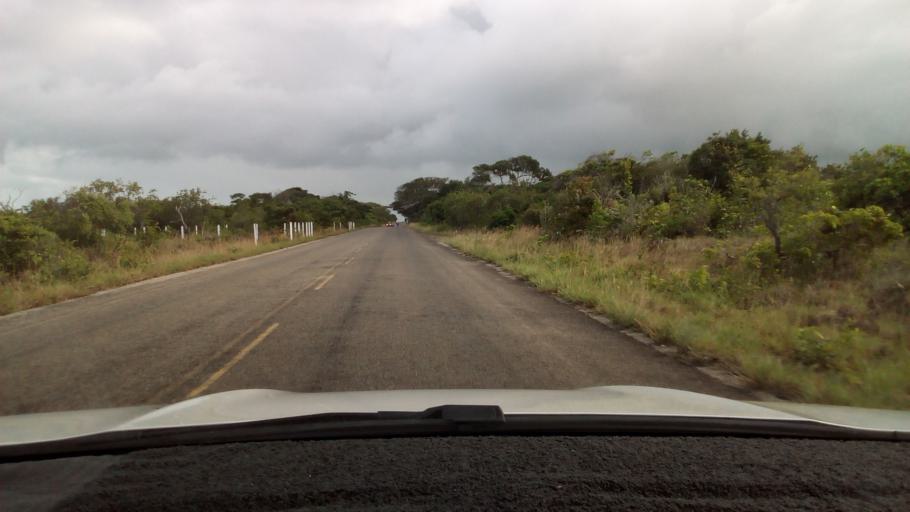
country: BR
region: Paraiba
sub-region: Conde
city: Conde
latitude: -7.3240
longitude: -34.8082
